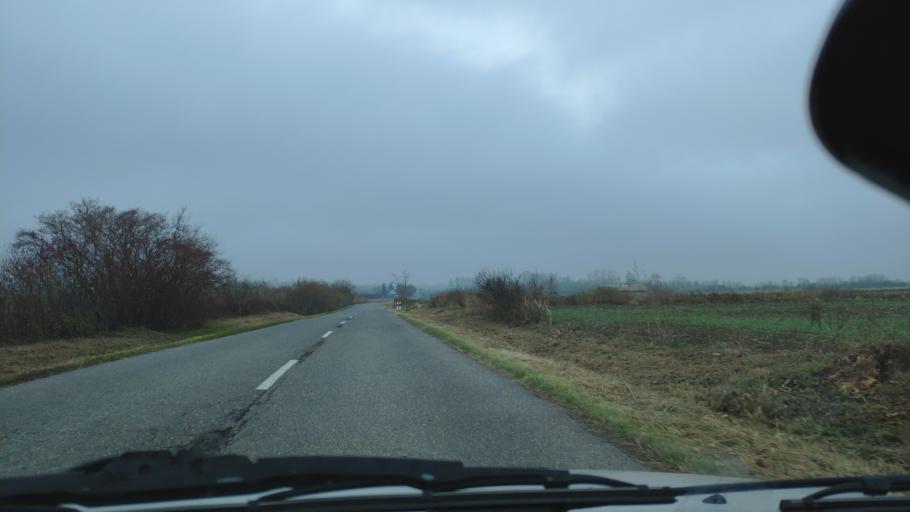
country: HU
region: Zala
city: Zalakomar
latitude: 46.5485
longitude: 17.1521
